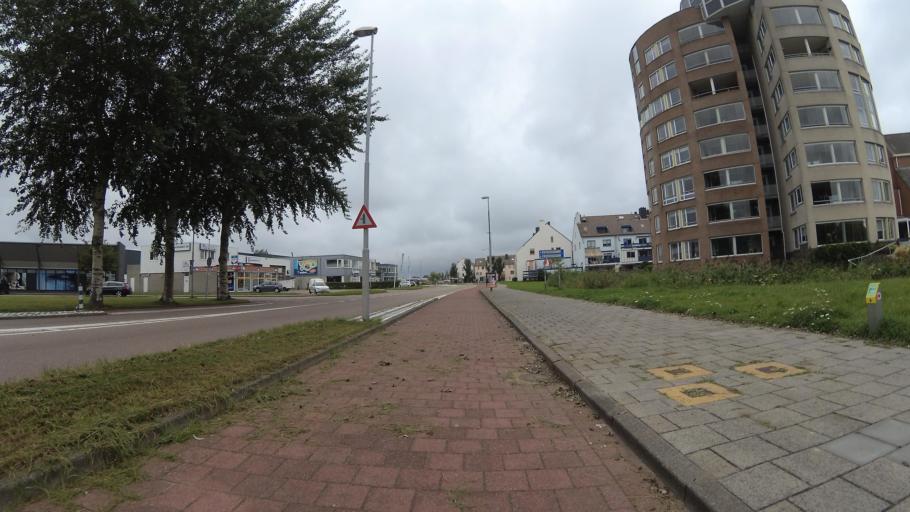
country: NL
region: North Holland
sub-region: Gemeente Den Helder
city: Den Helder
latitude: 52.9432
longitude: 4.7773
